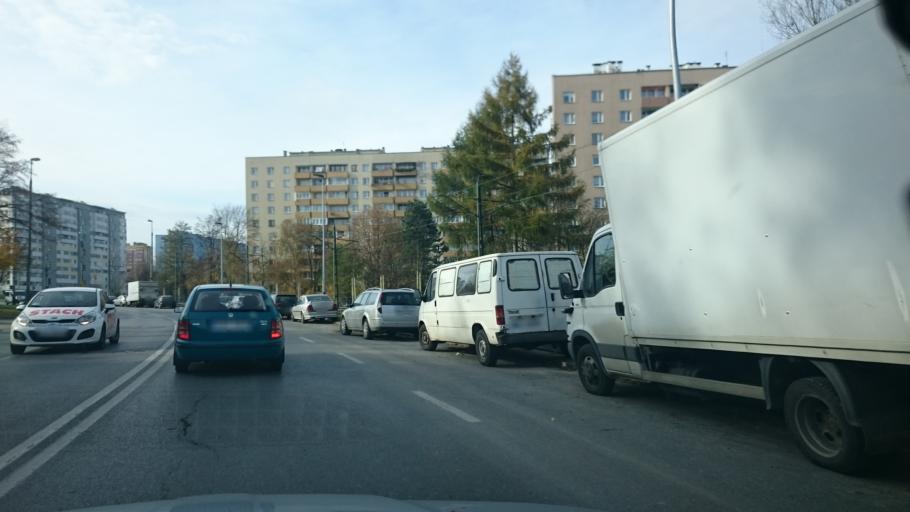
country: PL
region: Lesser Poland Voivodeship
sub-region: Powiat wielicki
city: Czarnochowice
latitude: 50.0167
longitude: 20.0053
